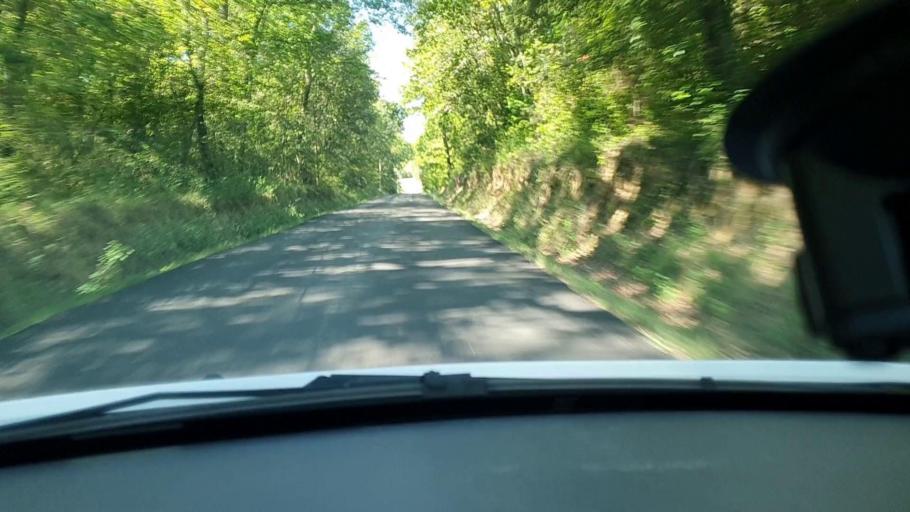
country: FR
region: Languedoc-Roussillon
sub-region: Departement du Gard
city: Goudargues
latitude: 44.1756
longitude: 4.5016
